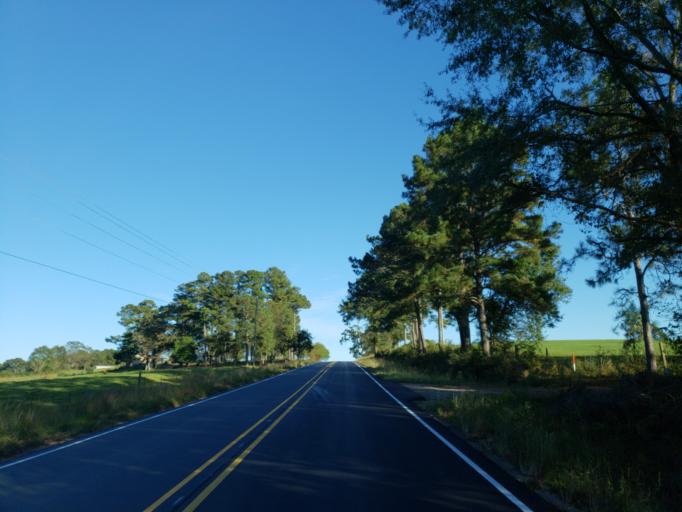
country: US
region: Mississippi
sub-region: Perry County
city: Richton
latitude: 31.3586
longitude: -88.7945
